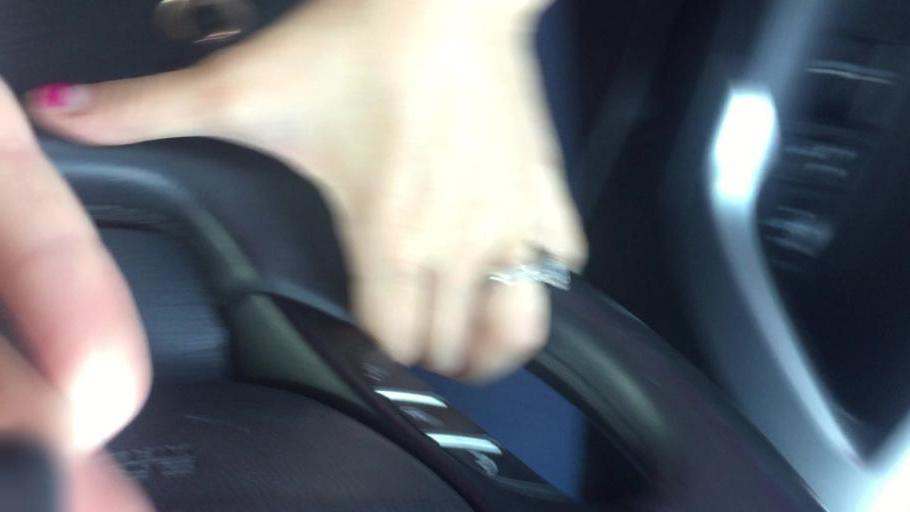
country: US
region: Texas
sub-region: Dallas County
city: Farmers Branch
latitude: 32.8957
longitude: -96.8561
